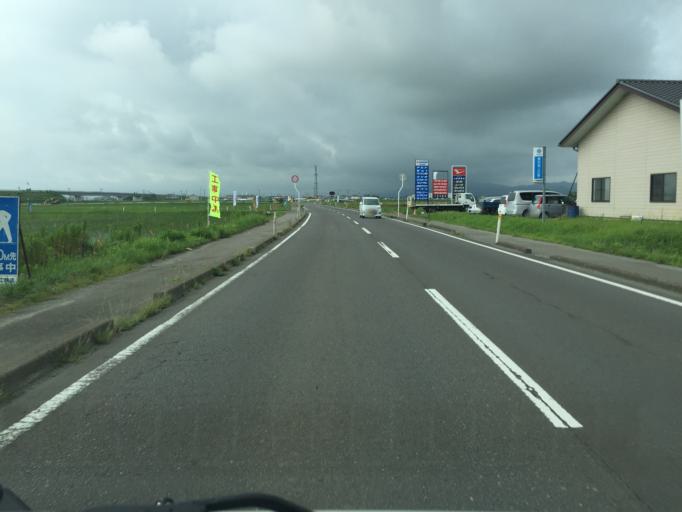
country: JP
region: Miyagi
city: Watari
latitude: 38.0396
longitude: 140.8898
